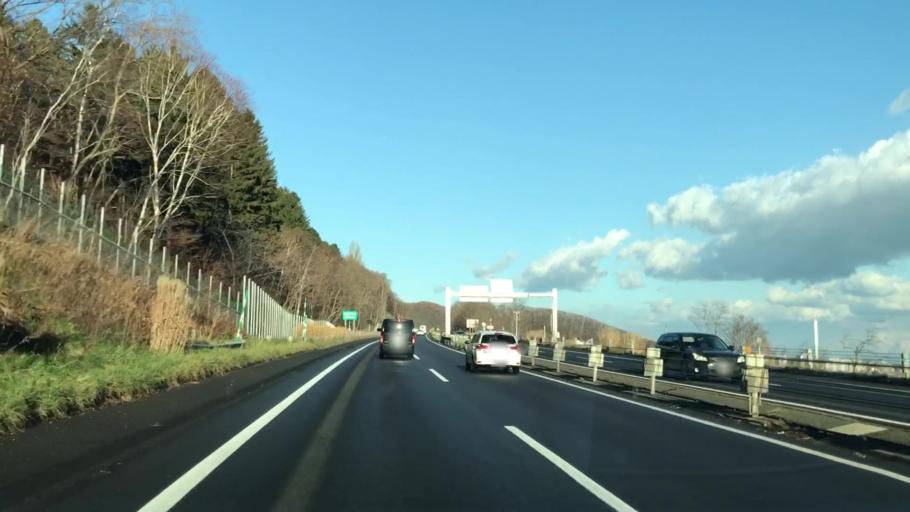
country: JP
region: Hokkaido
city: Sapporo
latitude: 43.0957
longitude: 141.2528
